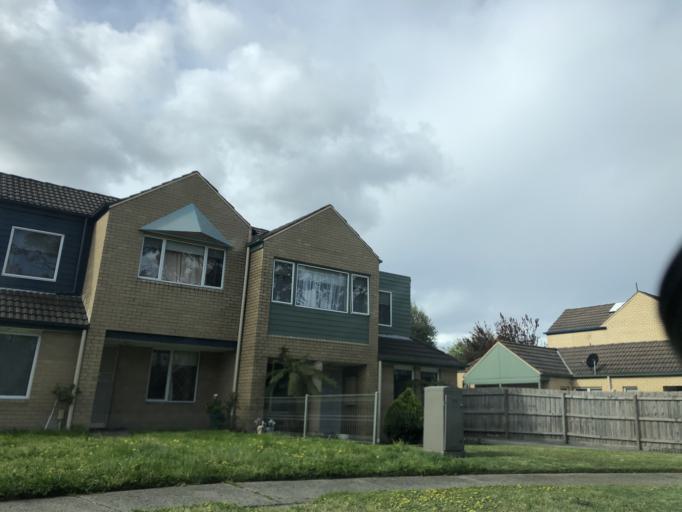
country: AU
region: Victoria
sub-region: Kingston
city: Clayton South
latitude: -37.9357
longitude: 145.1063
